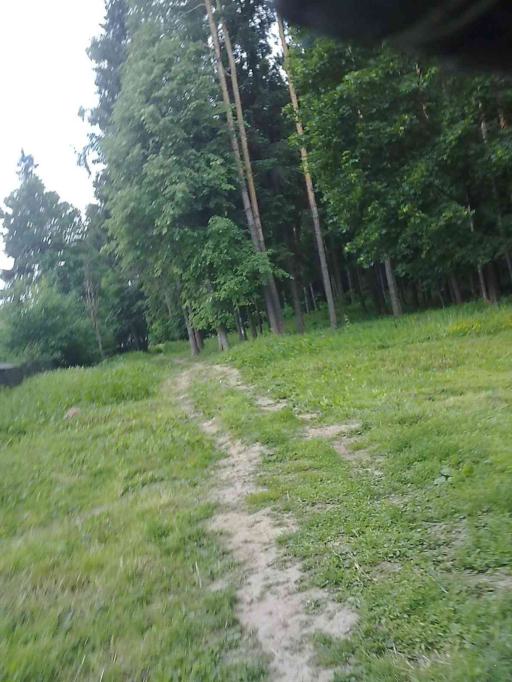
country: RU
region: Moskovskaya
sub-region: Leninskiy Rayon
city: Vnukovo
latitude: 55.6319
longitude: 37.3044
